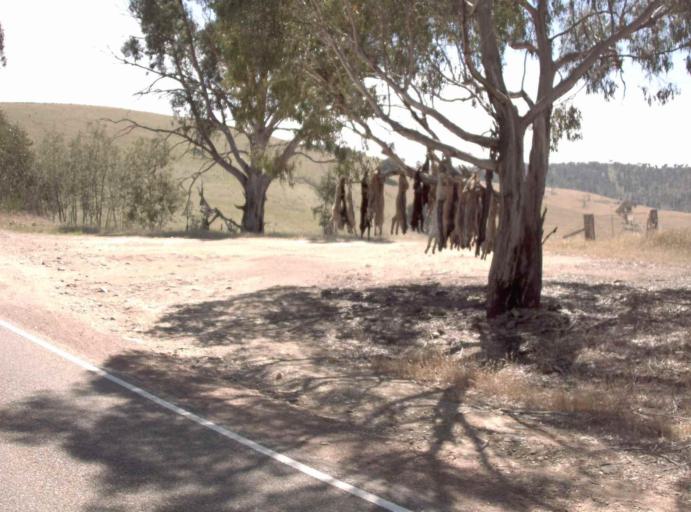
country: AU
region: Victoria
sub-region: Alpine
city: Mount Beauty
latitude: -37.0464
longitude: 147.6224
